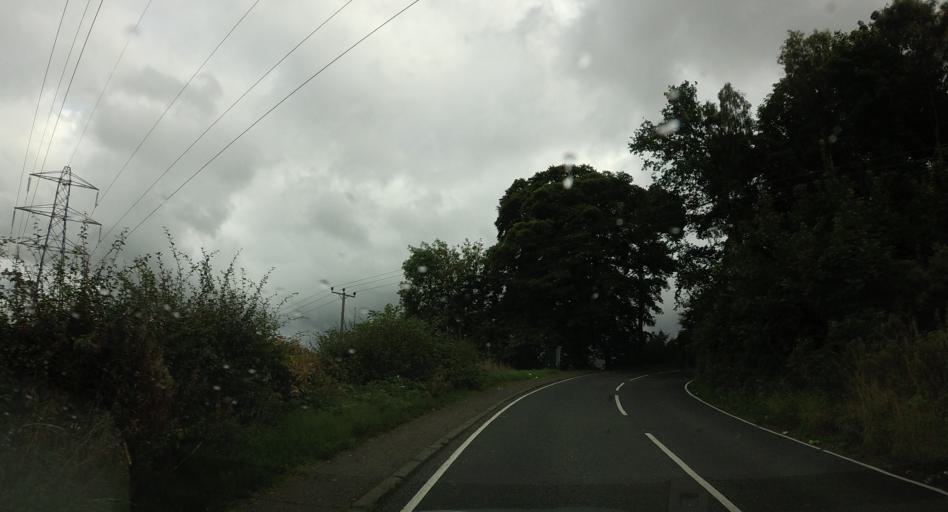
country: GB
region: Scotland
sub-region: Clackmannanshire
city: Alloa
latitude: 56.1350
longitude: -3.7953
